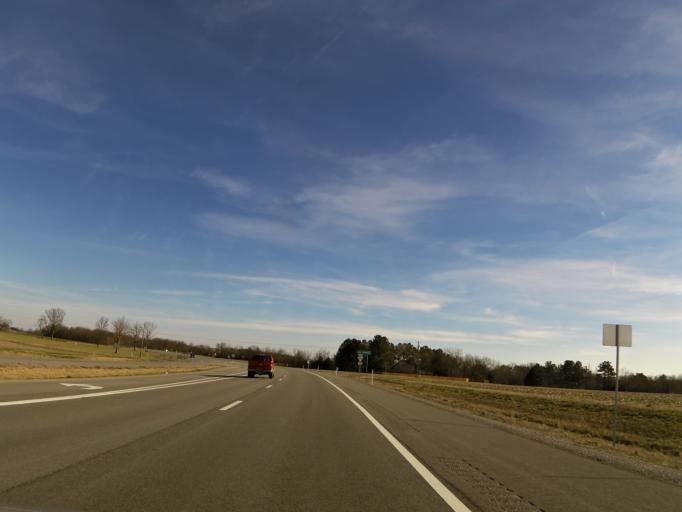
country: US
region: Tennessee
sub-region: Cannon County
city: Woodbury
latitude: 35.7688
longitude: -85.9755
